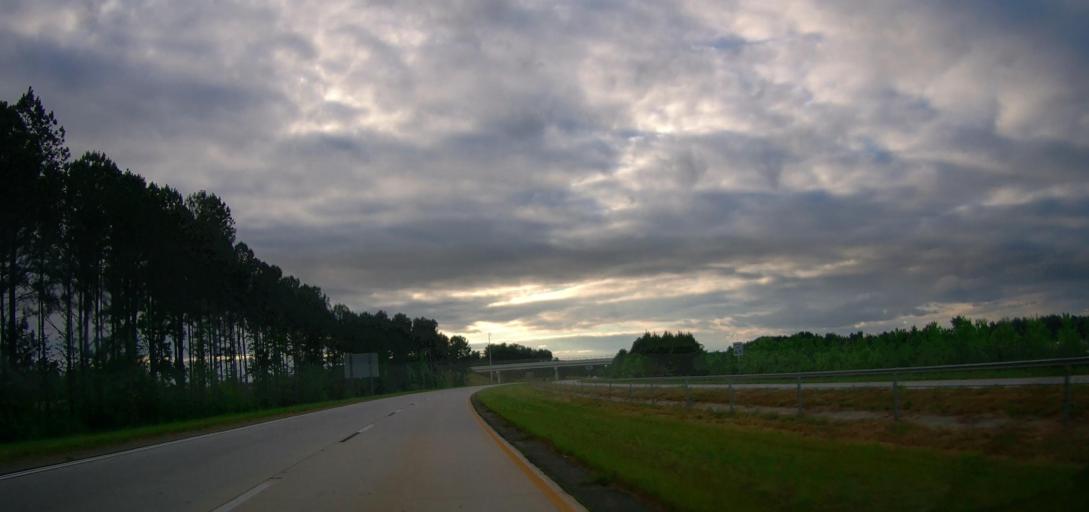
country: US
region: Georgia
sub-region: Oconee County
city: Watkinsville
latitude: 33.9147
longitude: -83.4575
